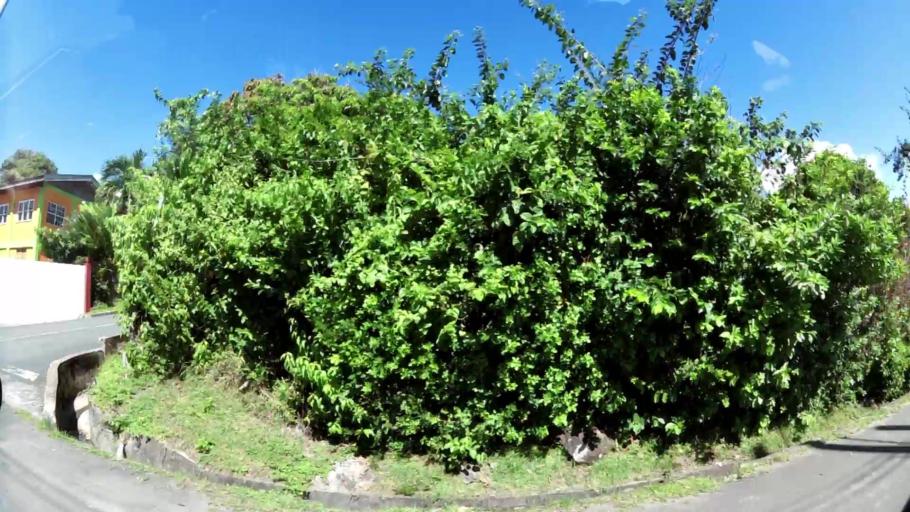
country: TT
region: Tobago
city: Scarborough
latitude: 11.1665
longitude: -60.7568
